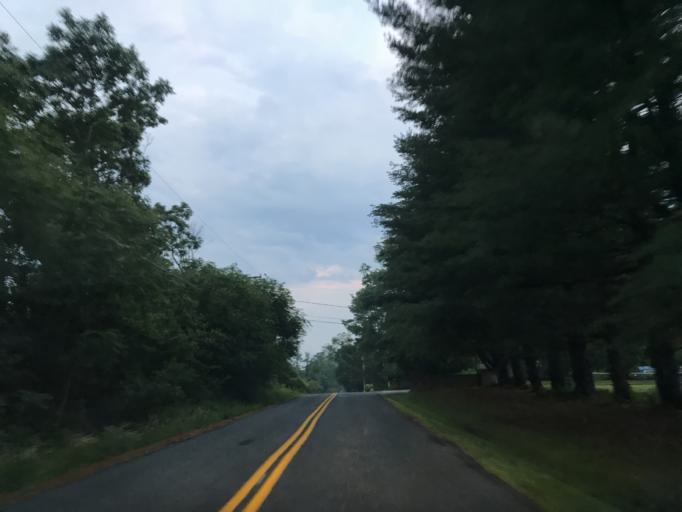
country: US
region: Maryland
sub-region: Harford County
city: Fallston
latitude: 39.4980
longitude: -76.4155
